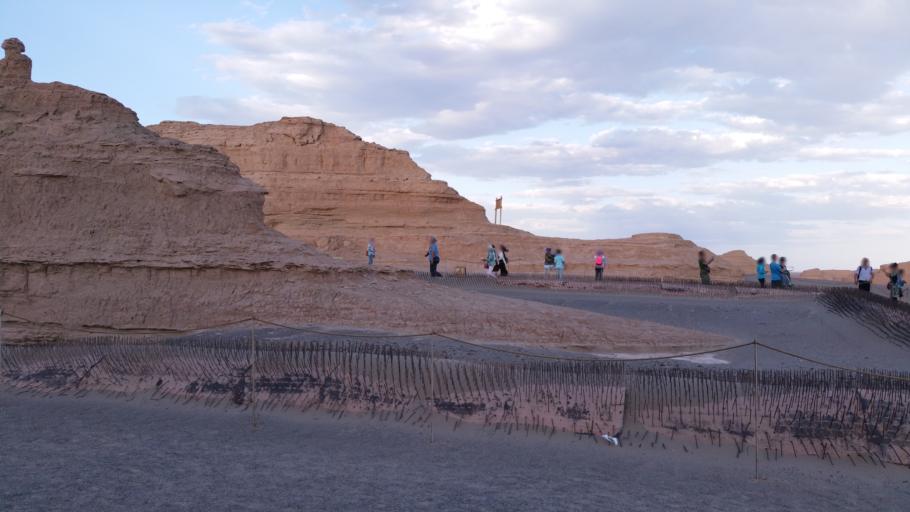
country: CN
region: Heilongjiang Sheng
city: Duobagou
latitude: 40.5422
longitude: 93.1125
